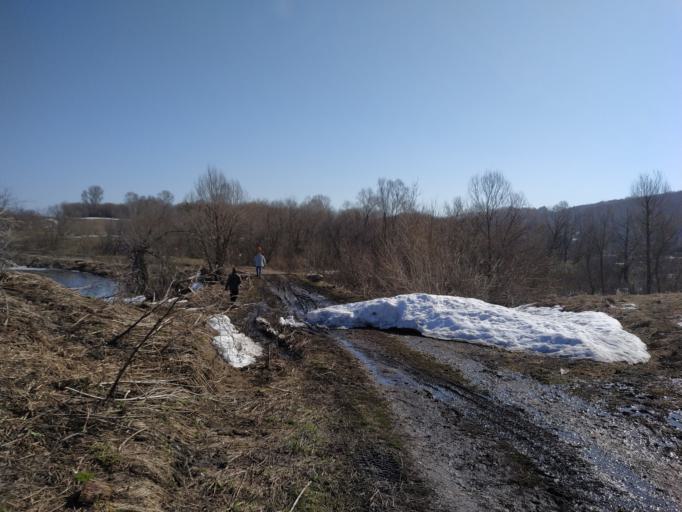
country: RU
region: Altai Krai
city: Krasnogorskoye
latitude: 52.4823
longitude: 86.2246
